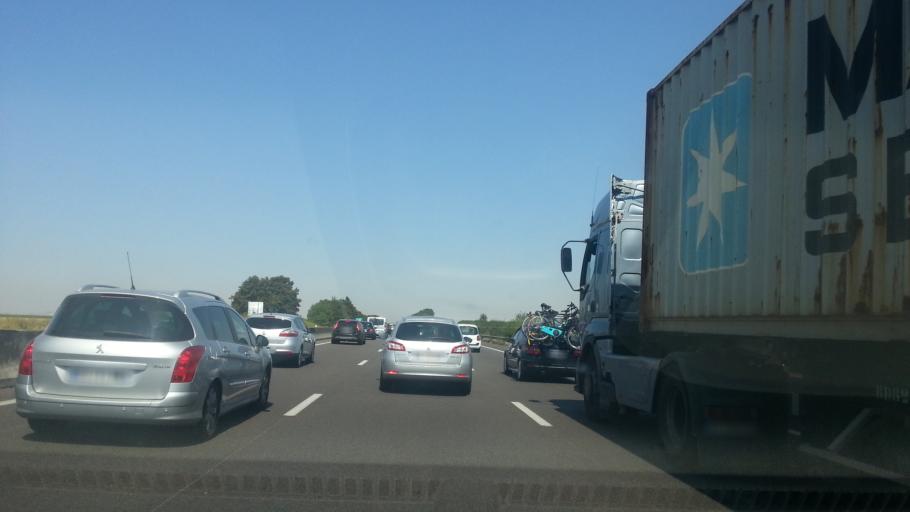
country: FR
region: Centre
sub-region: Departement du Loiret
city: Gidy
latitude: 47.9931
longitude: 1.8554
